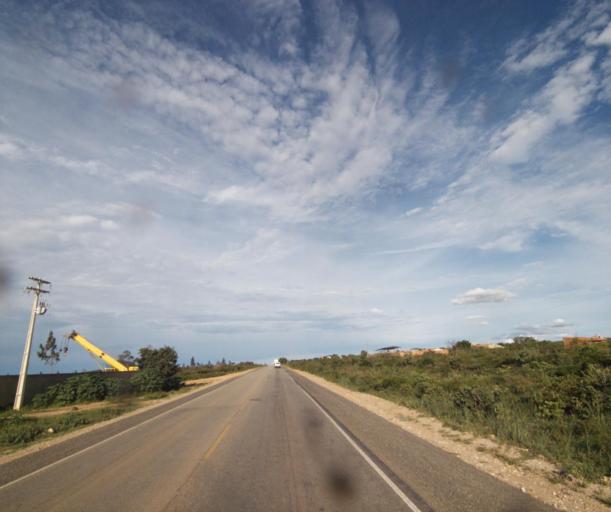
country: BR
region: Bahia
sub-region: Caetite
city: Caetite
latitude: -14.0686
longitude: -42.5327
